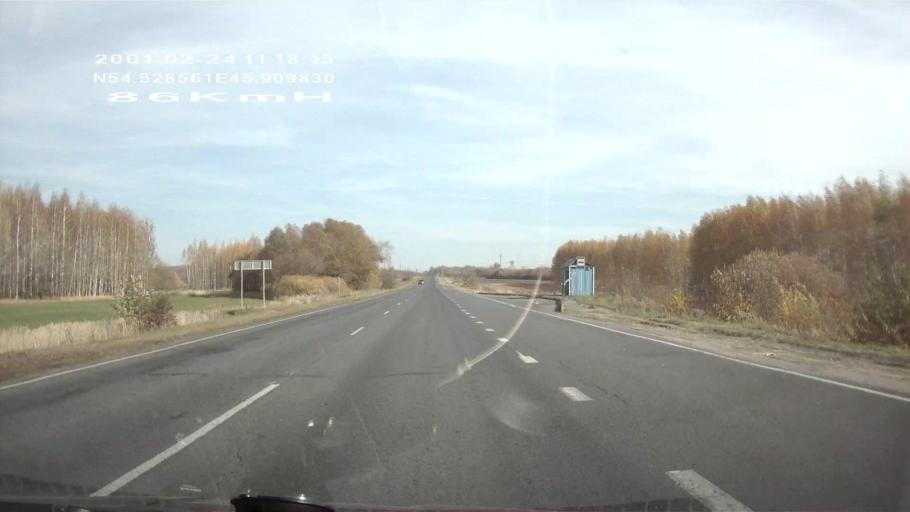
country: RU
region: Mordoviya
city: Atyashevo
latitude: 54.5285
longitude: 45.9097
